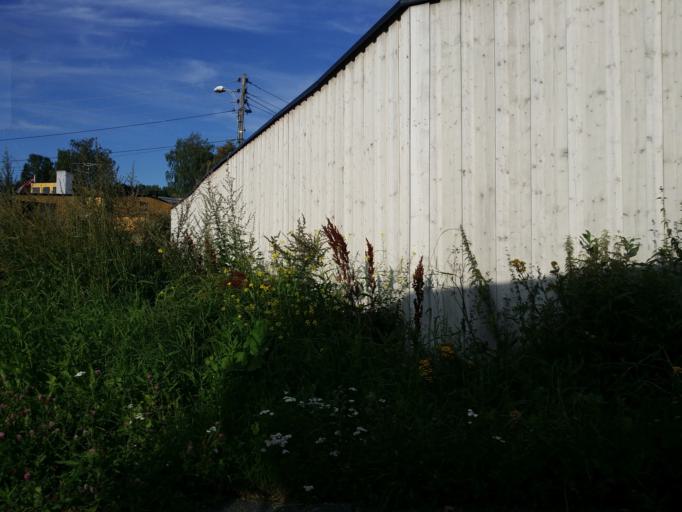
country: NO
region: Oslo
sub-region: Oslo
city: Oslo
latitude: 59.9103
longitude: 10.8493
